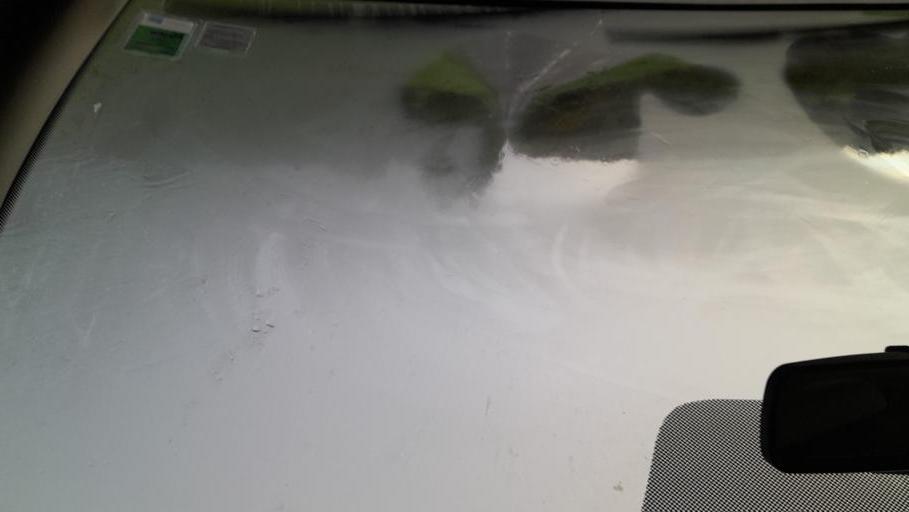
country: FR
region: Pays de la Loire
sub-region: Departement de la Mayenne
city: Ballots
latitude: 47.8731
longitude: -1.0469
